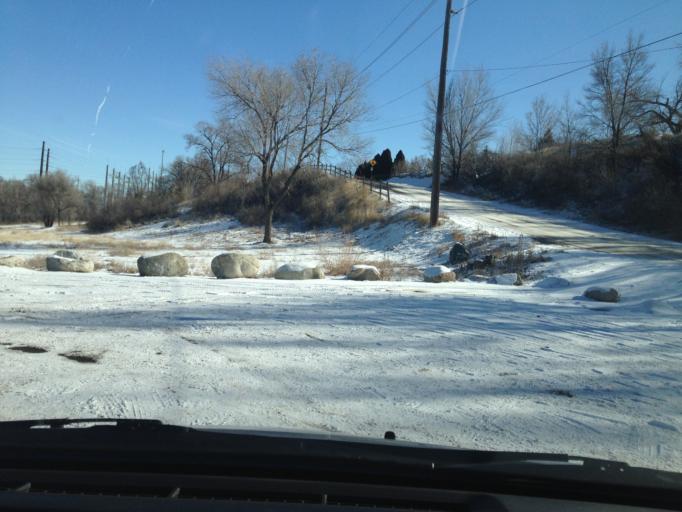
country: US
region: Colorado
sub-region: Adams County
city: Berkley
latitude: 39.7972
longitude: -105.0339
